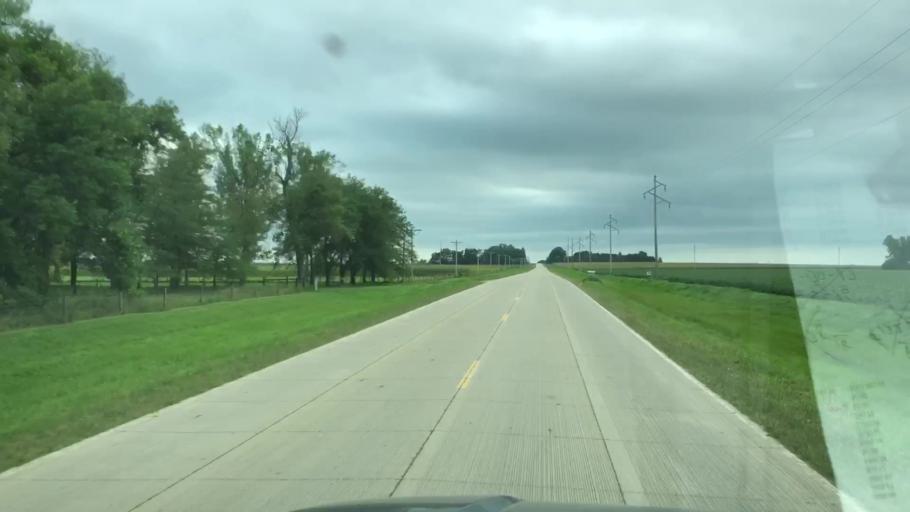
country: US
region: Iowa
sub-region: O'Brien County
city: Sheldon
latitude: 43.1770
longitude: -95.9801
